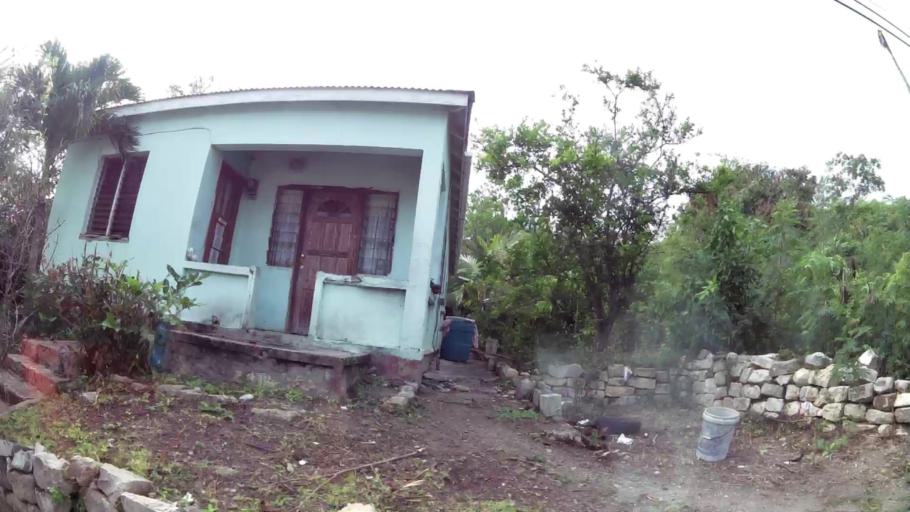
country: AG
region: Saint Peter
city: Parham
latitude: 17.0577
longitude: -61.7263
